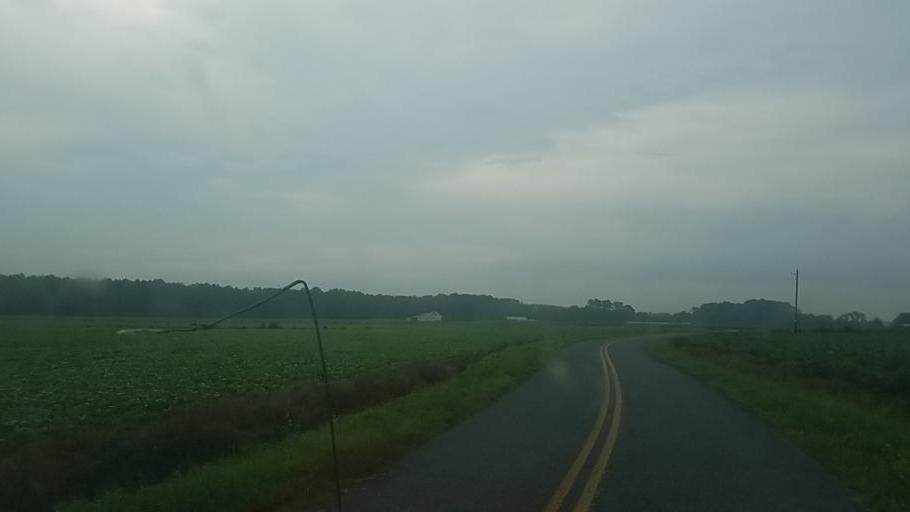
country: US
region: Maryland
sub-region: Wicomico County
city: Pittsville
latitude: 38.4245
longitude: -75.3199
